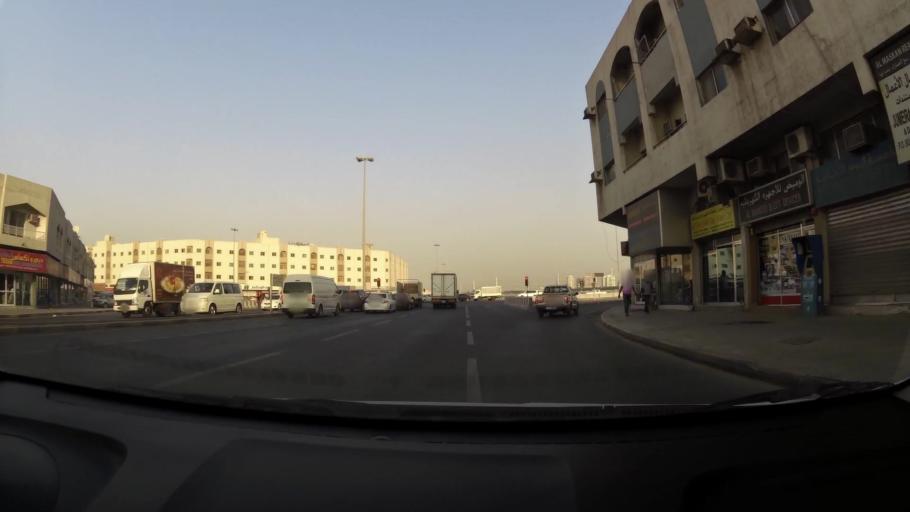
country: AE
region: Ash Shariqah
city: Sharjah
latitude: 25.3024
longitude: 55.3978
